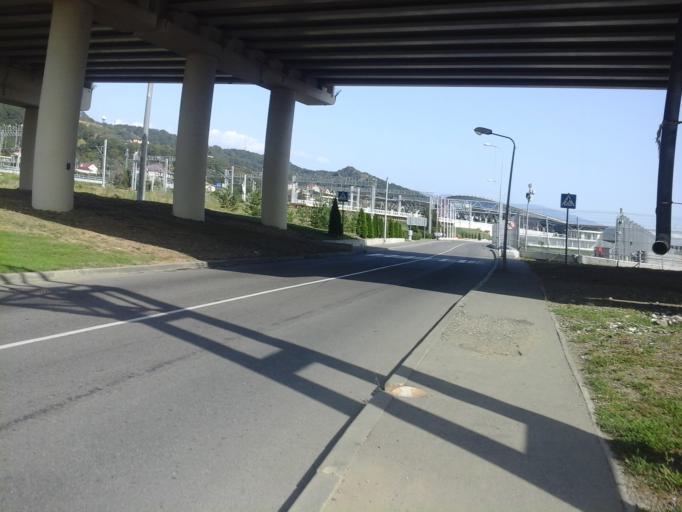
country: RU
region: Krasnodarskiy
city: Adler
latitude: 43.4133
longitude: 39.9679
